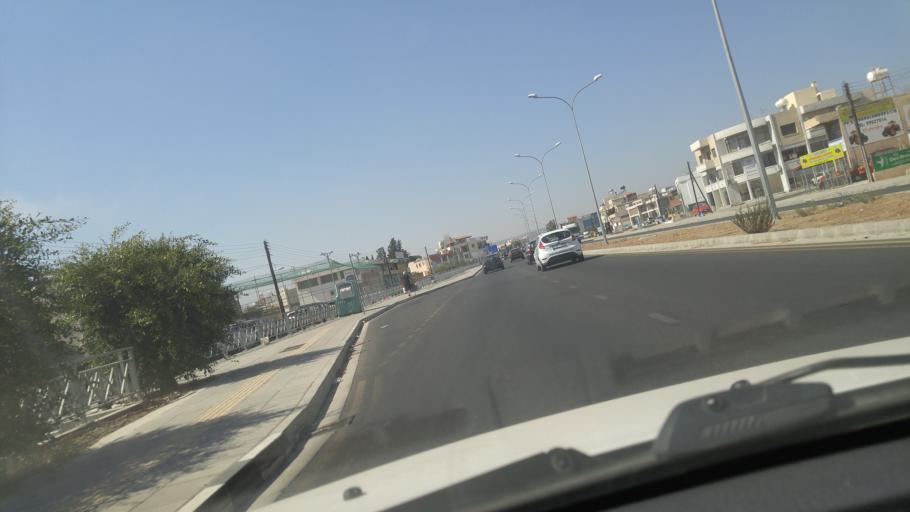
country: CY
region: Limassol
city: Pano Polemidia
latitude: 34.6788
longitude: 32.9950
